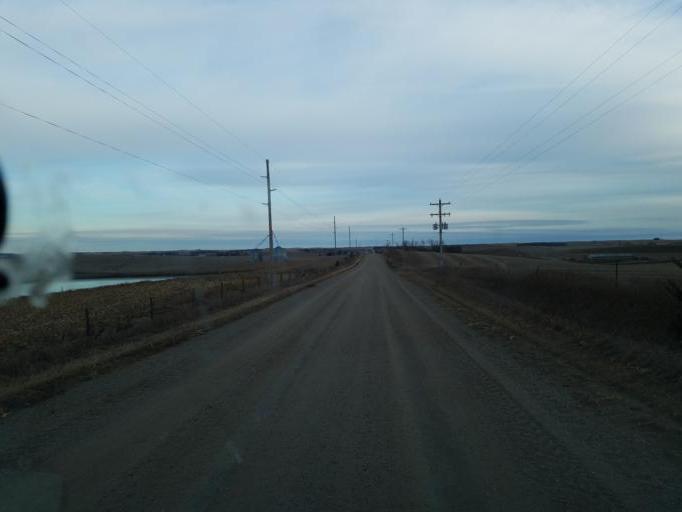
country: US
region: Nebraska
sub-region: Knox County
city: Bloomfield
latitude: 42.5791
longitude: -97.6228
